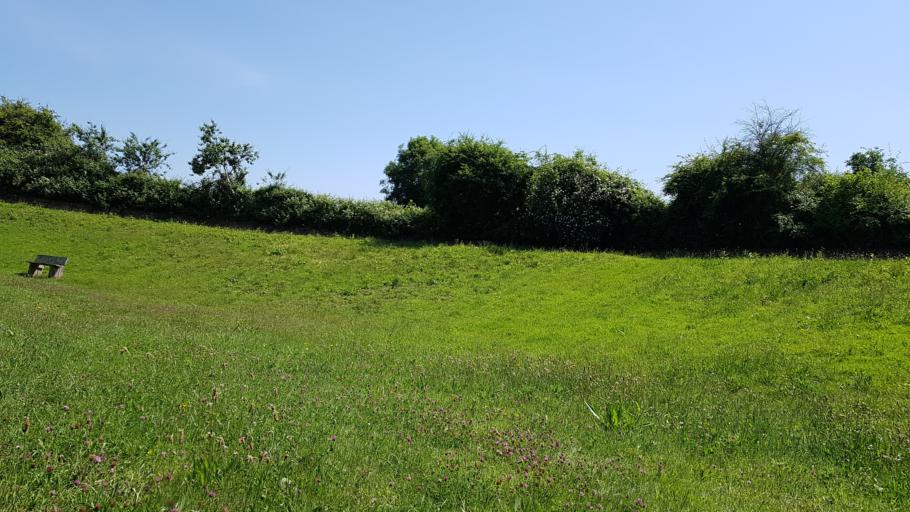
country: GB
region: England
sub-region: Isle of Wight
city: Cowes
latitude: 50.7583
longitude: -1.3036
